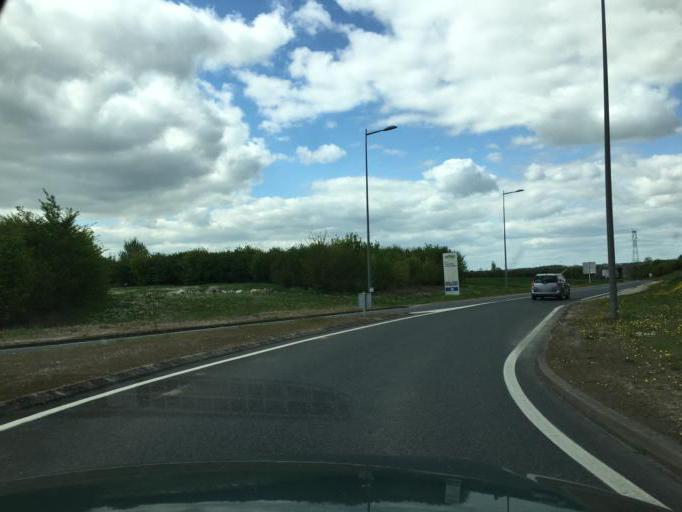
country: FR
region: Centre
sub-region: Departement du Loir-et-Cher
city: Mer
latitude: 47.7232
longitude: 1.5007
